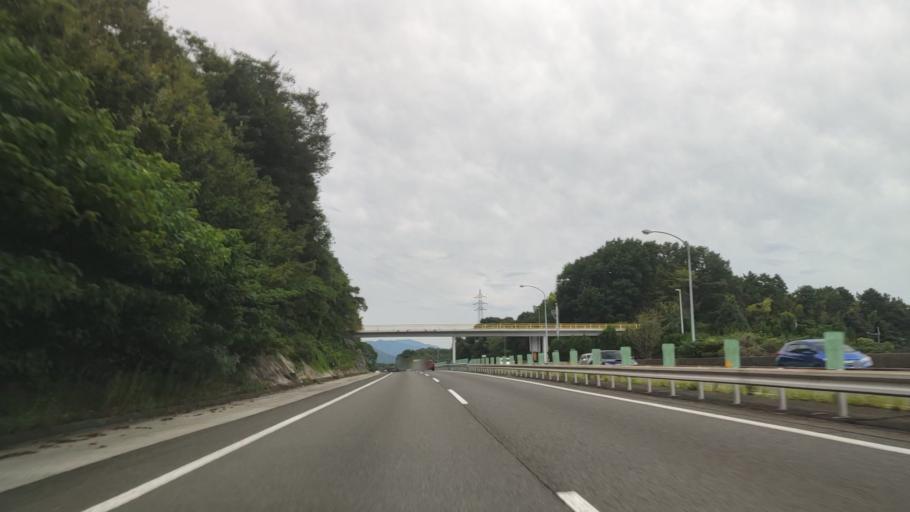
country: JP
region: Shiga Prefecture
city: Hikone
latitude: 35.2576
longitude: 136.2792
